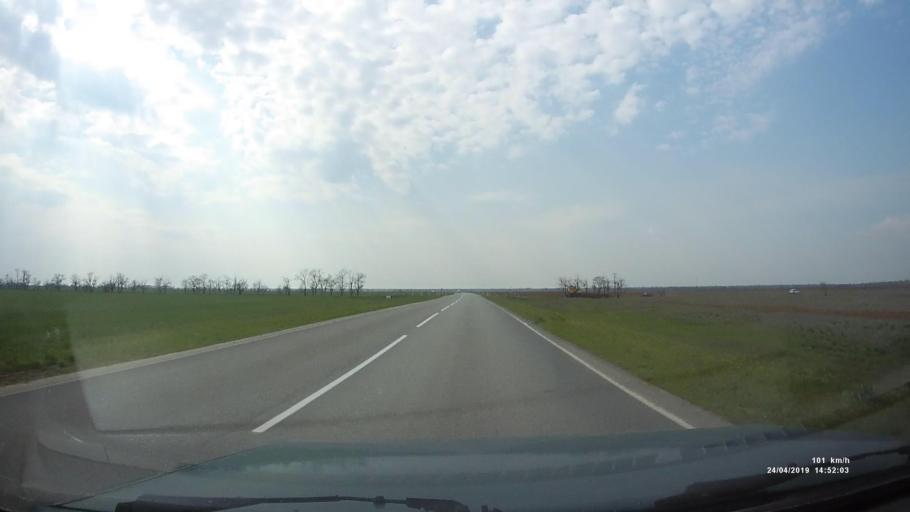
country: RU
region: Rostov
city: Remontnoye
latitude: 46.5291
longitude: 43.6887
